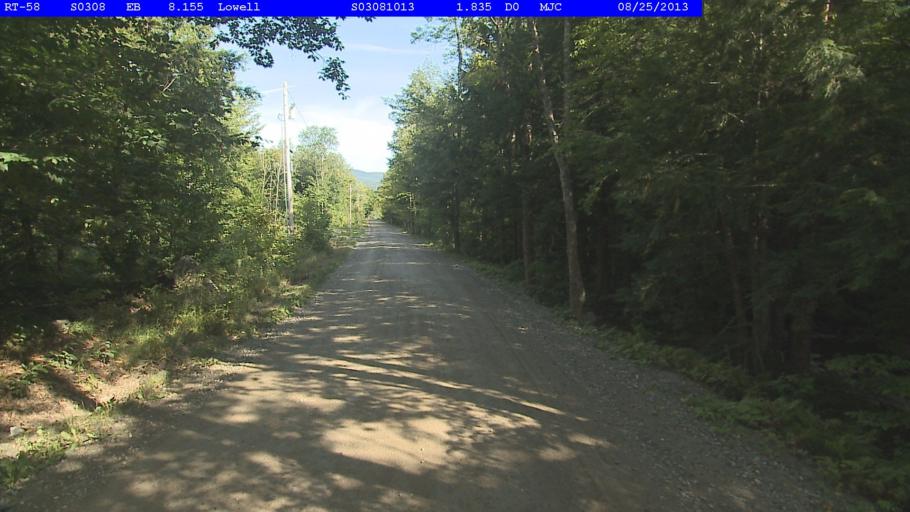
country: US
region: Vermont
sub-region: Franklin County
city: Richford
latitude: 44.8198
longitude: -72.4796
